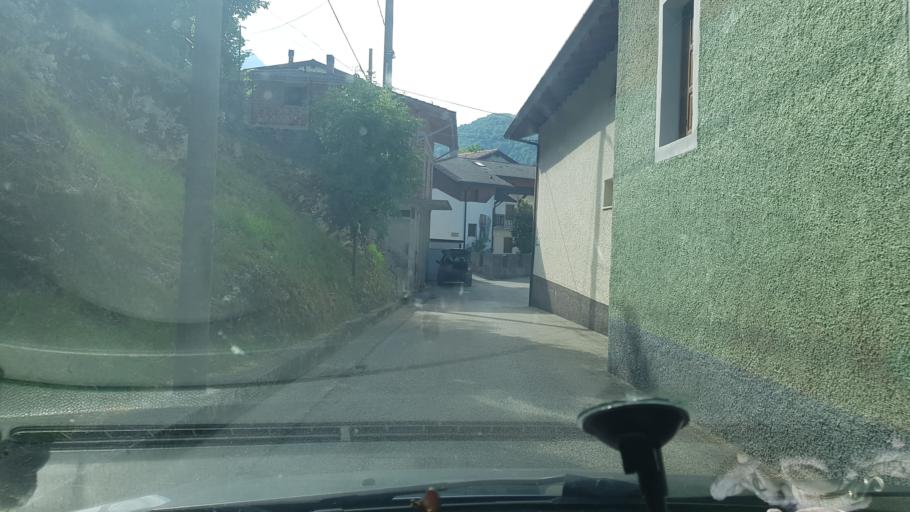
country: IT
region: Friuli Venezia Giulia
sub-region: Provincia di Udine
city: Prato
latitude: 46.3619
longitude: 13.3537
